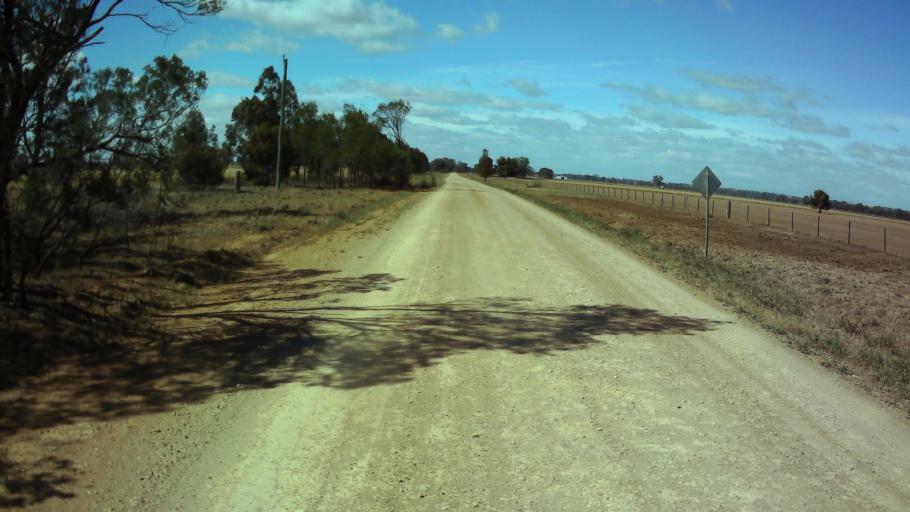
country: AU
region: New South Wales
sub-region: Weddin
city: Grenfell
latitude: -34.0175
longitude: 148.3197
